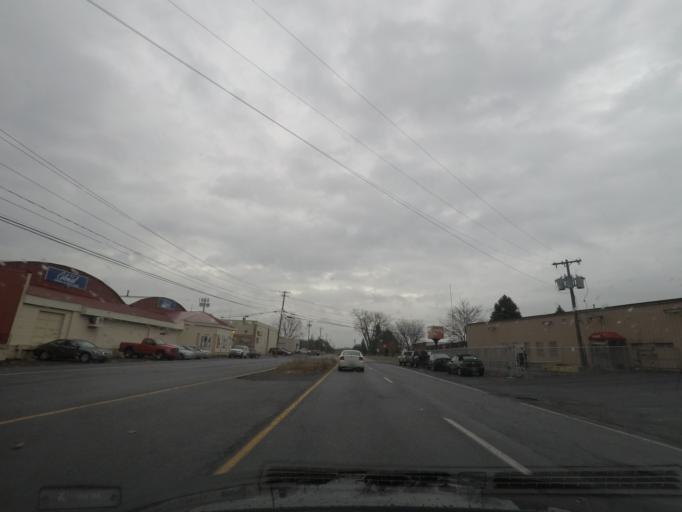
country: US
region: New York
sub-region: Albany County
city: Colonie
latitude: 42.7032
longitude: -73.8293
